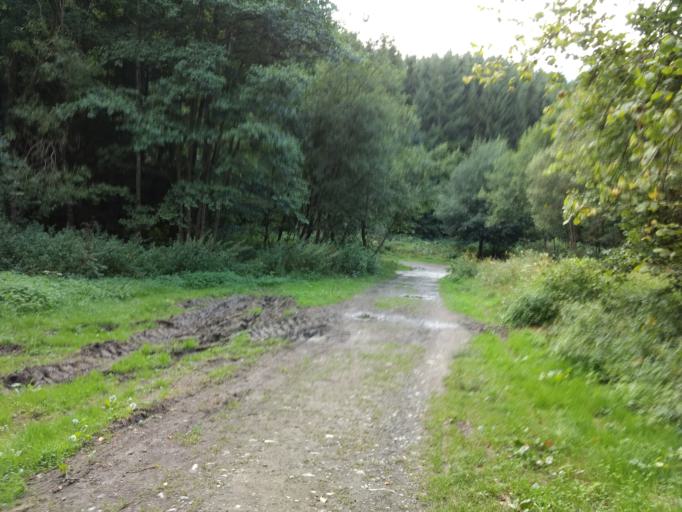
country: BE
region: Wallonia
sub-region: Province du Luxembourg
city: Houffalize
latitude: 50.1481
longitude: 5.7278
